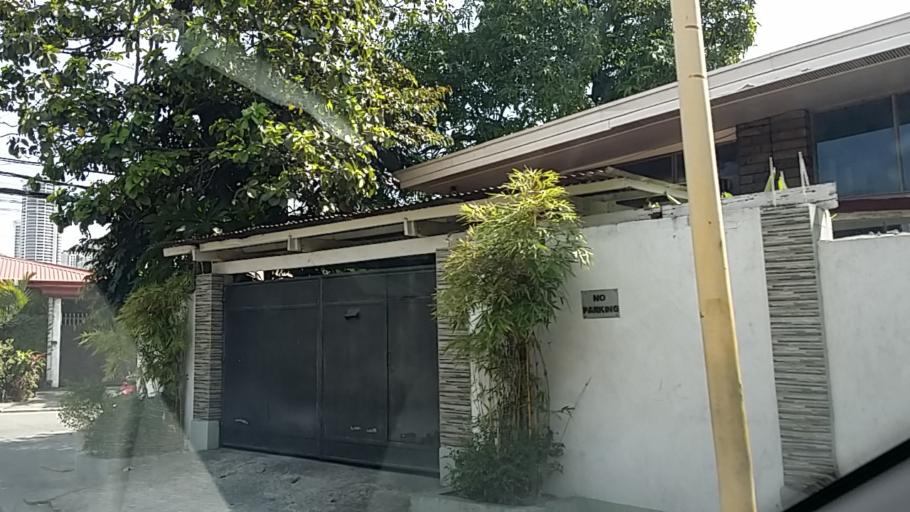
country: PH
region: Metro Manila
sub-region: Mandaluyong
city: Mandaluyong City
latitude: 14.5754
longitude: 121.0365
